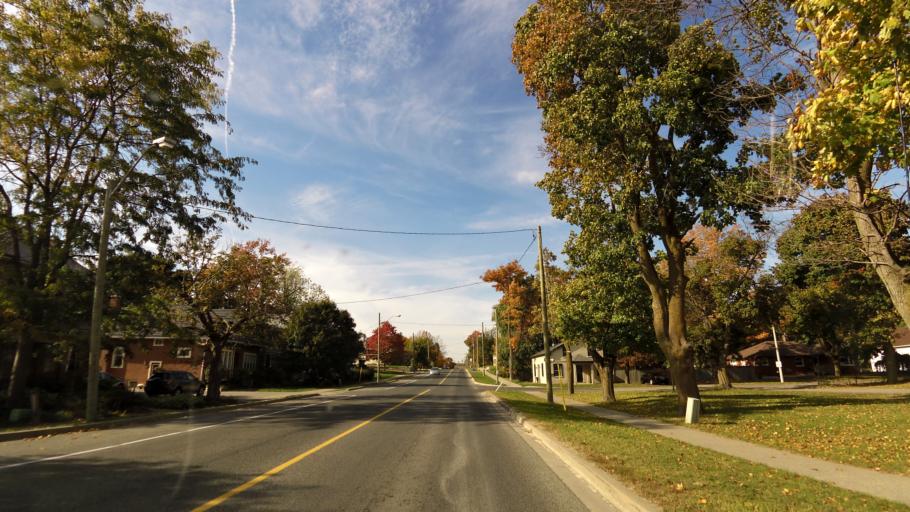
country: CA
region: Ontario
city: Orangeville
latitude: 43.7730
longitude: -80.0677
